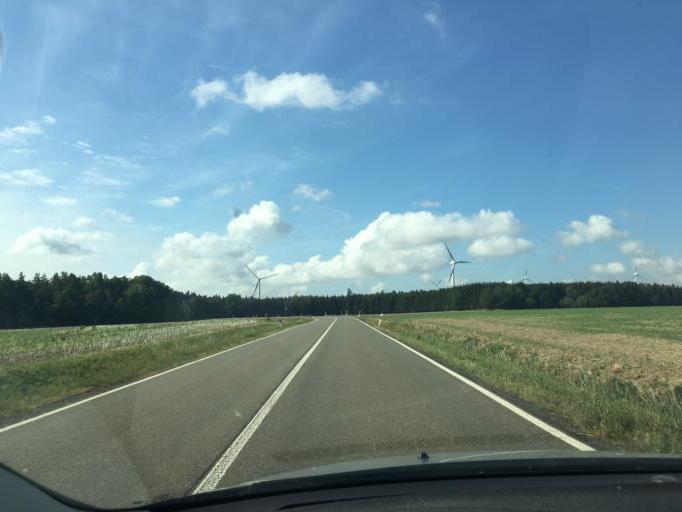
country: DE
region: Thuringia
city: Mittelpollnitz
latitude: 50.7306
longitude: 11.9097
